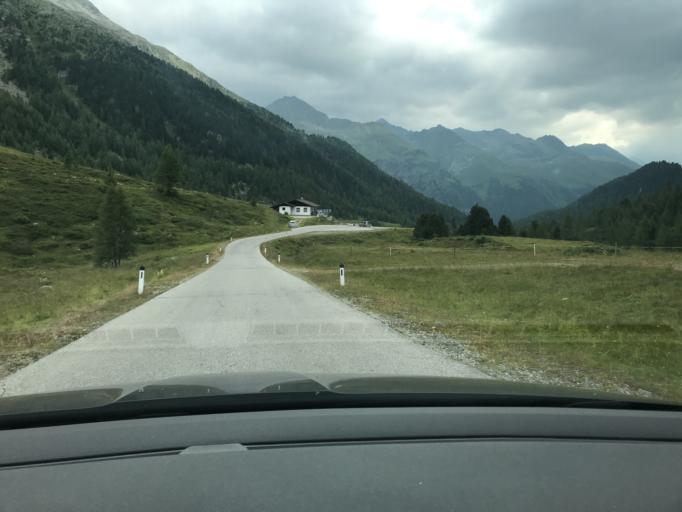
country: IT
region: Trentino-Alto Adige
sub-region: Bolzano
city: San Martino
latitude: 46.8961
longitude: 12.2172
